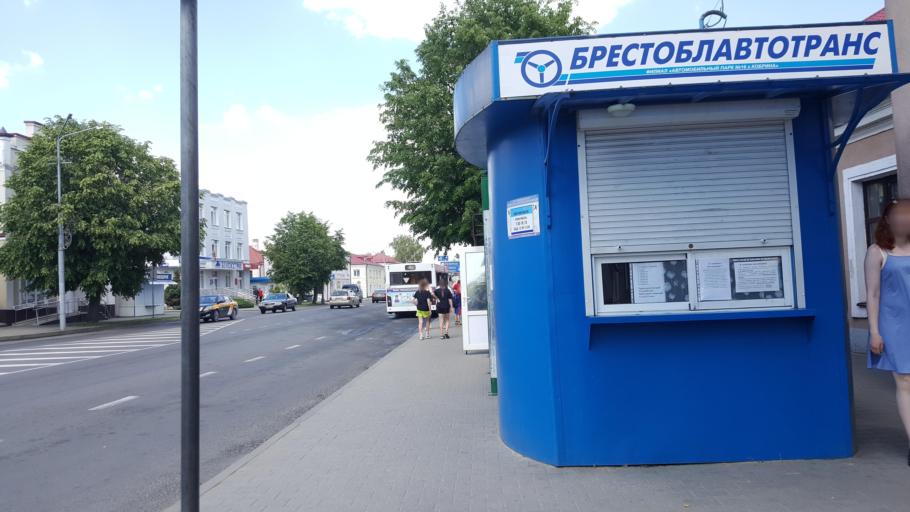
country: BY
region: Brest
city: Kobryn
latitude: 52.2123
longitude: 24.3568
